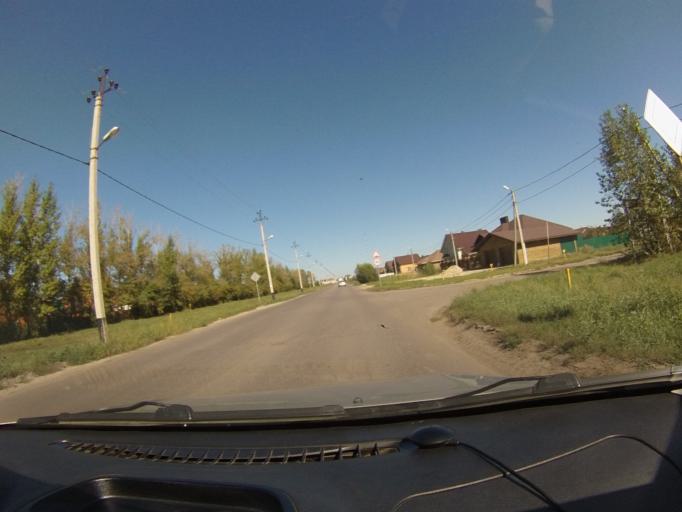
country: RU
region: Tambov
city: Tambov
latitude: 52.7724
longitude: 41.3757
